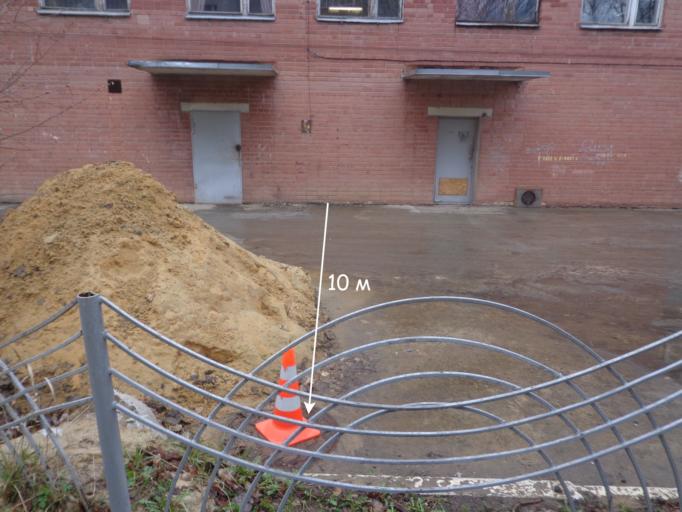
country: RU
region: Voronezj
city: Voronezh
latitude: 51.7209
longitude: 39.2175
